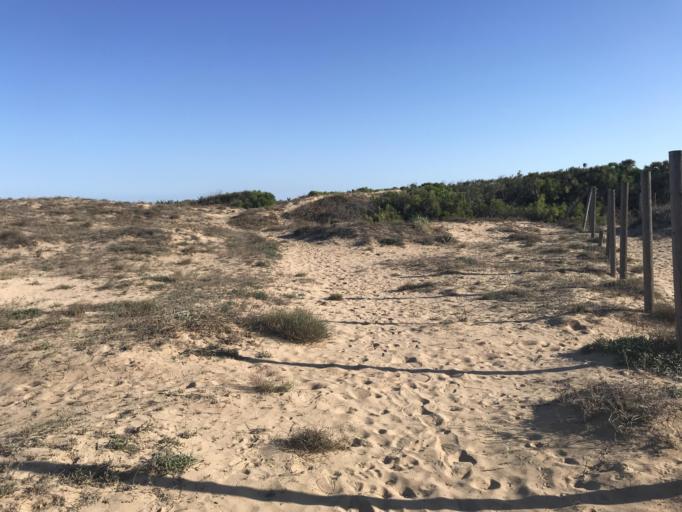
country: ES
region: Valencia
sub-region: Provincia de Alicante
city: Guardamar del Segura
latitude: 38.0313
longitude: -0.6518
